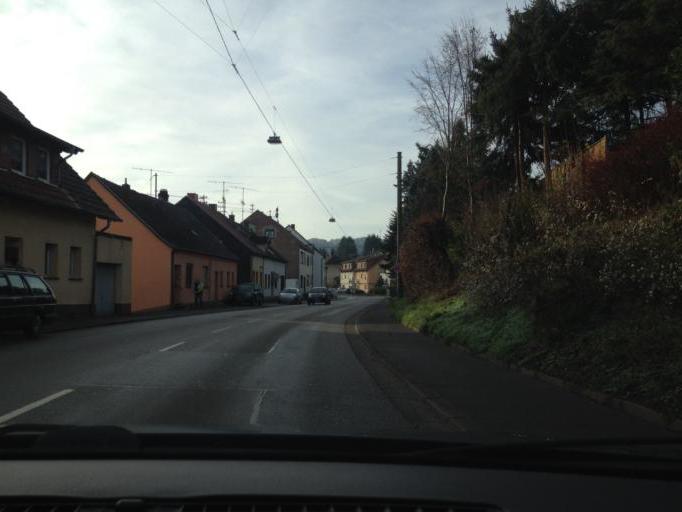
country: DE
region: Saarland
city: Sankt Wendel
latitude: 49.4563
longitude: 7.1524
